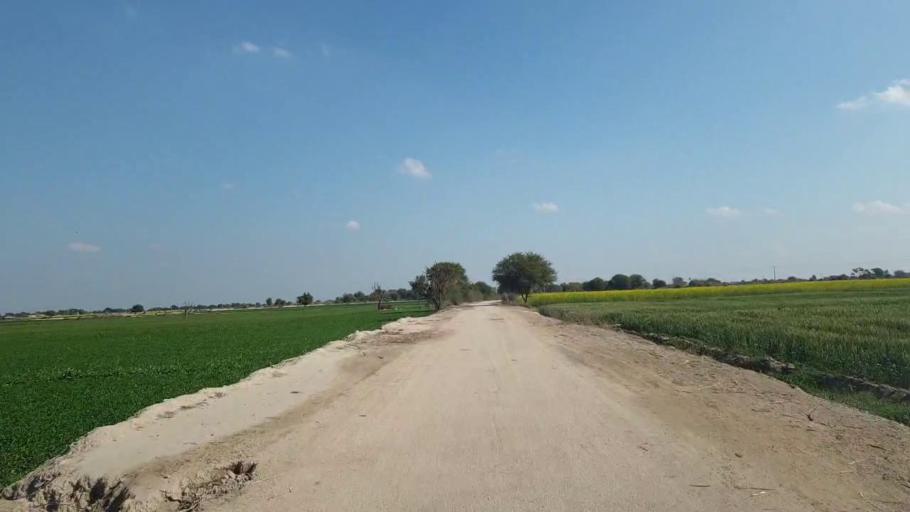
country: PK
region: Sindh
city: Shahpur Chakar
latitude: 26.0901
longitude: 68.5757
